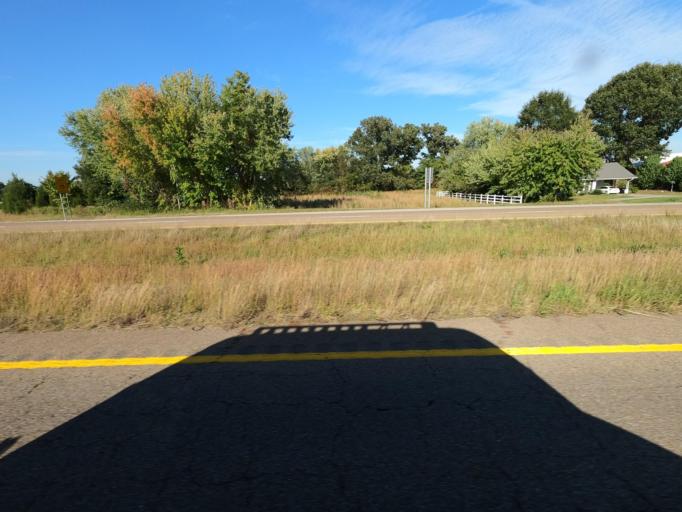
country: US
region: Tennessee
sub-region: Crockett County
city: Bells
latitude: 35.7461
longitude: -89.1004
